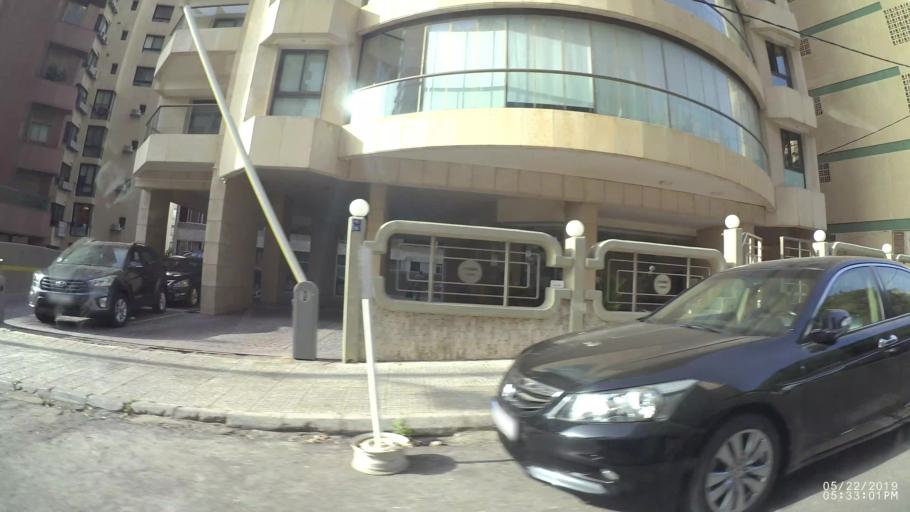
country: LB
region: Beyrouth
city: Ra's Bayrut
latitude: 33.8942
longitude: 35.4744
